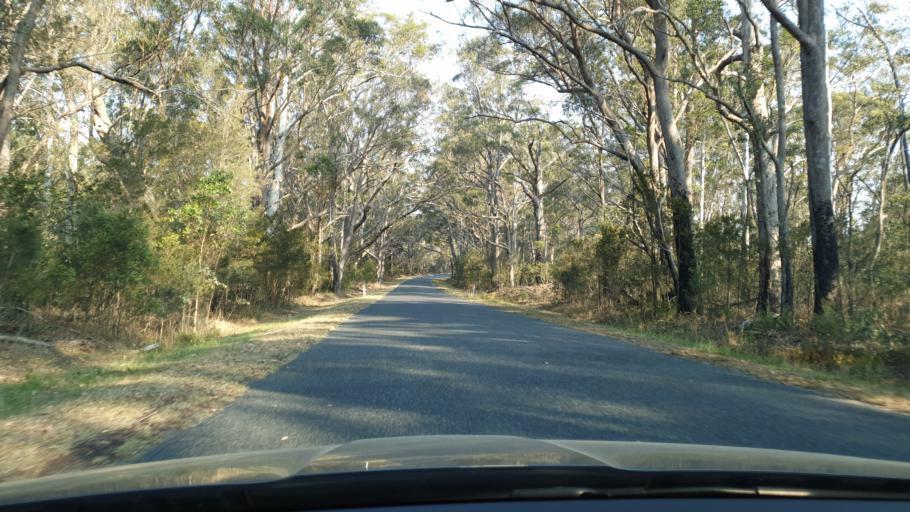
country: AU
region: New South Wales
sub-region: Tenterfield Municipality
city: Carrolls Creek
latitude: -28.6991
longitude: 152.0955
